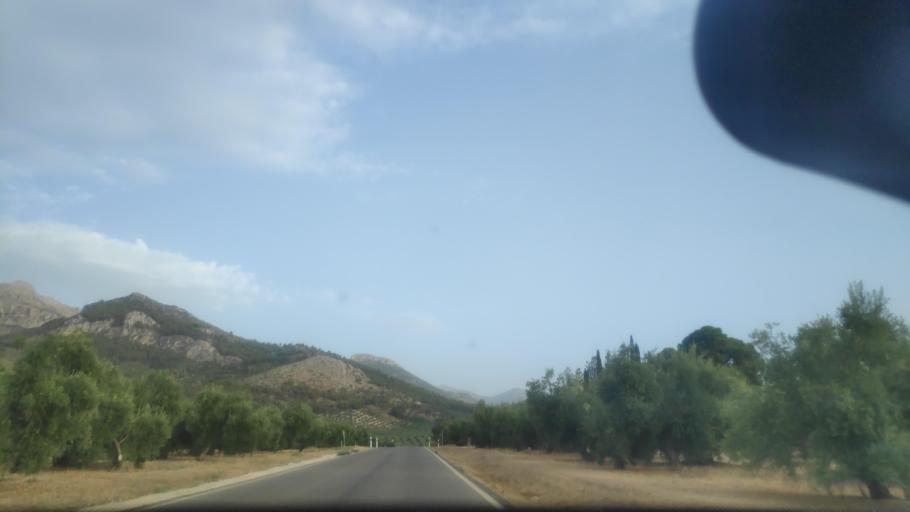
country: ES
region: Andalusia
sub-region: Provincia de Jaen
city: Jimena
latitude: 37.8339
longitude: -3.5281
